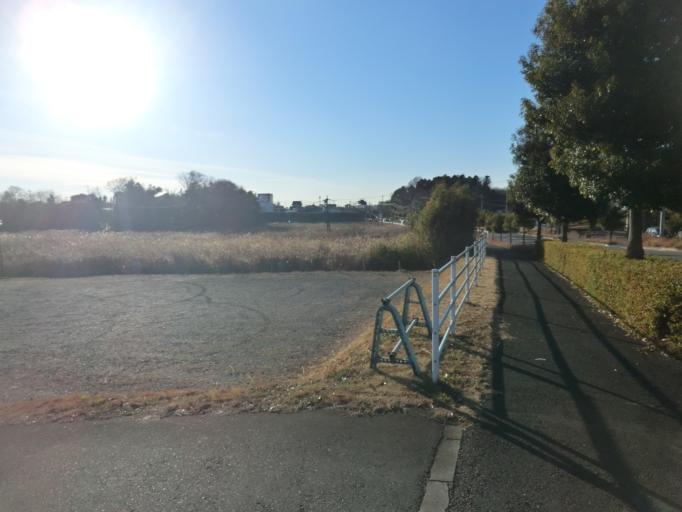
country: JP
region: Ibaraki
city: Mitsukaido
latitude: 35.9849
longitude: 139.9864
